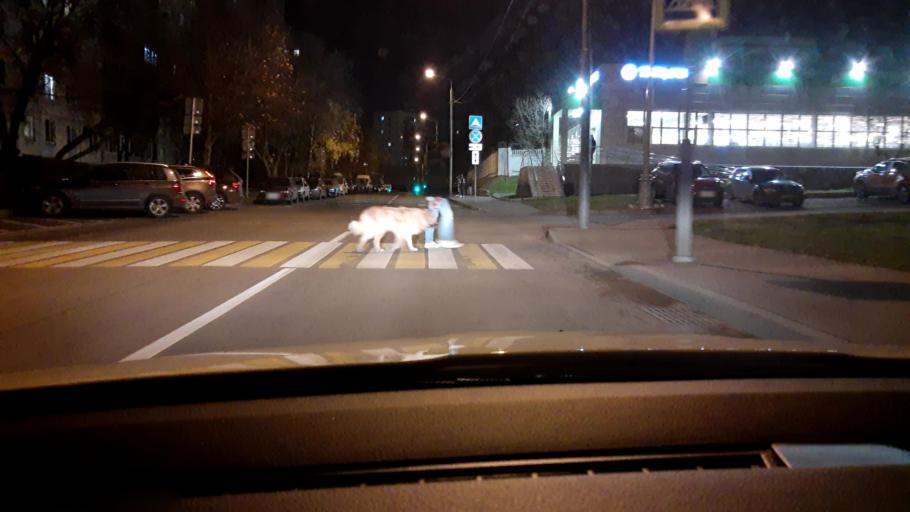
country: RU
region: Moscow
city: Strogino
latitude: 55.8570
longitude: 37.4071
